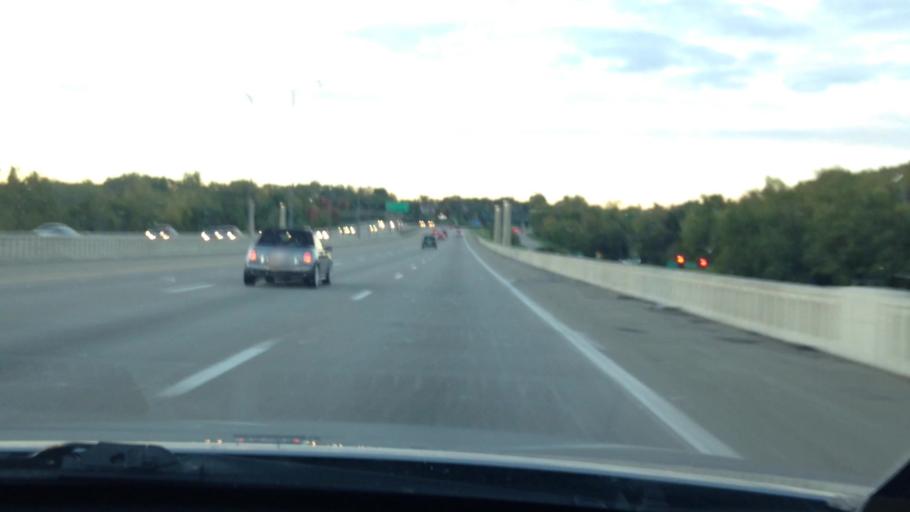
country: US
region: Kansas
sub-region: Johnson County
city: Westwood
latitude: 39.0415
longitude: -94.5593
